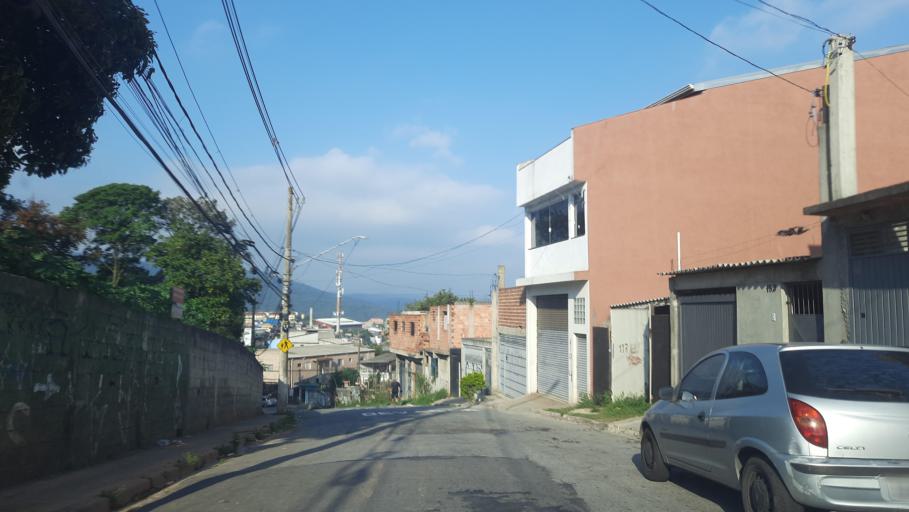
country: BR
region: Sao Paulo
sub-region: Caieiras
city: Caieiras
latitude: -23.4521
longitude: -46.7168
